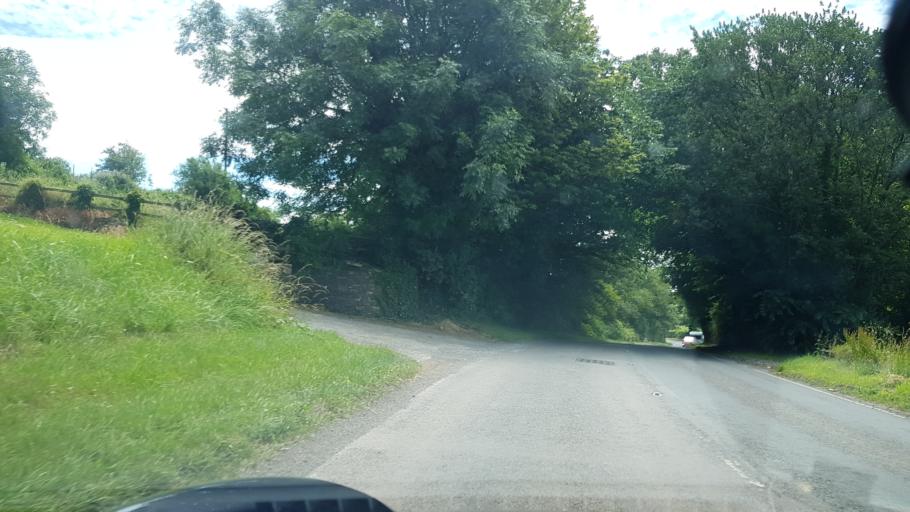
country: GB
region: Wales
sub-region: Carmarthenshire
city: Saint Clears
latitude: 51.7819
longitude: -4.4707
